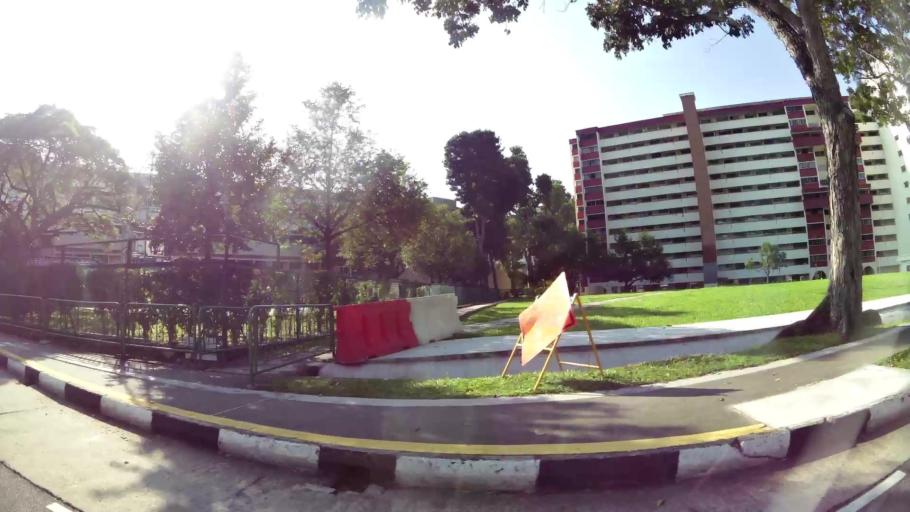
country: SG
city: Singapore
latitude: 1.3279
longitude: 103.9198
